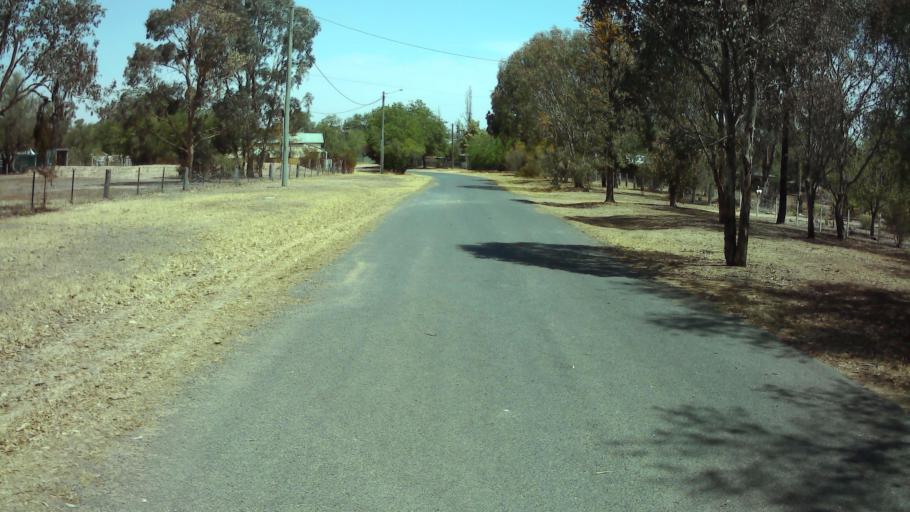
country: AU
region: New South Wales
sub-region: Weddin
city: Grenfell
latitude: -33.8876
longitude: 148.1539
